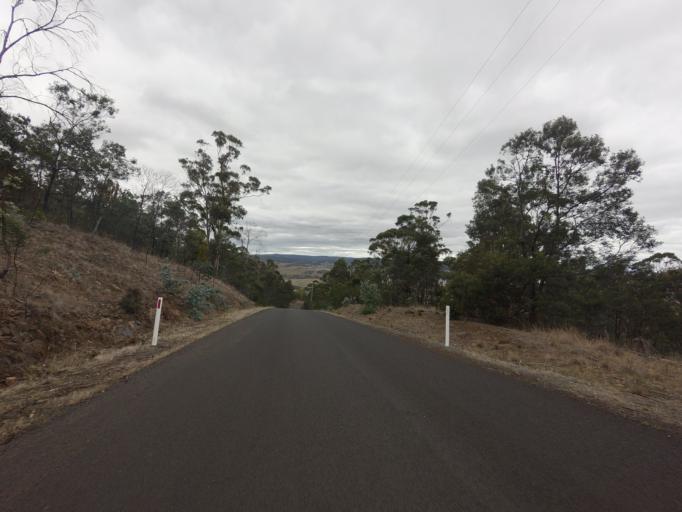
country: AU
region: Tasmania
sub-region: Clarence
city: Cambridge
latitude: -42.7916
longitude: 147.4053
